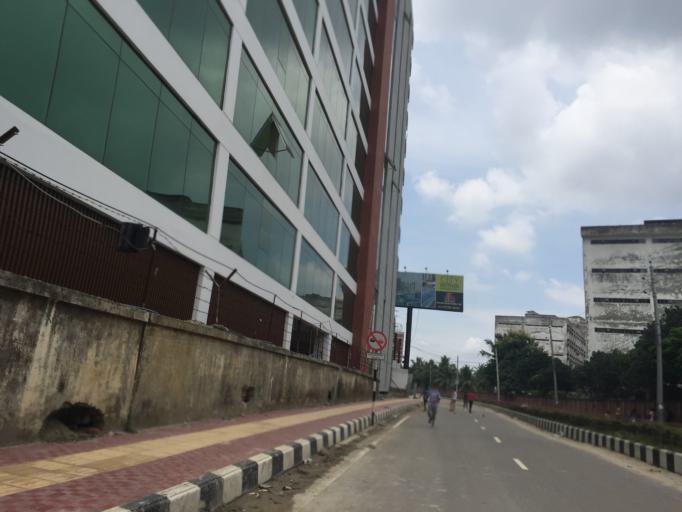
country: BD
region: Dhaka
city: Azimpur
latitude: 23.8042
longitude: 90.3823
